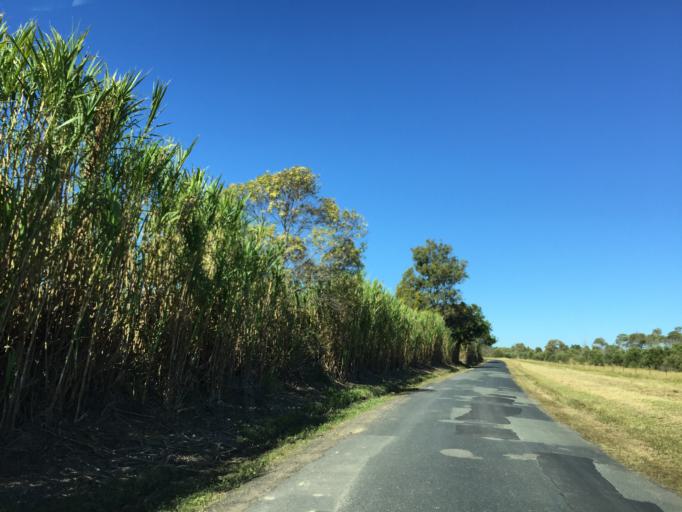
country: AU
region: Queensland
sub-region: Moreton Bay
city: Caboolture
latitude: -27.0211
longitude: 152.9855
